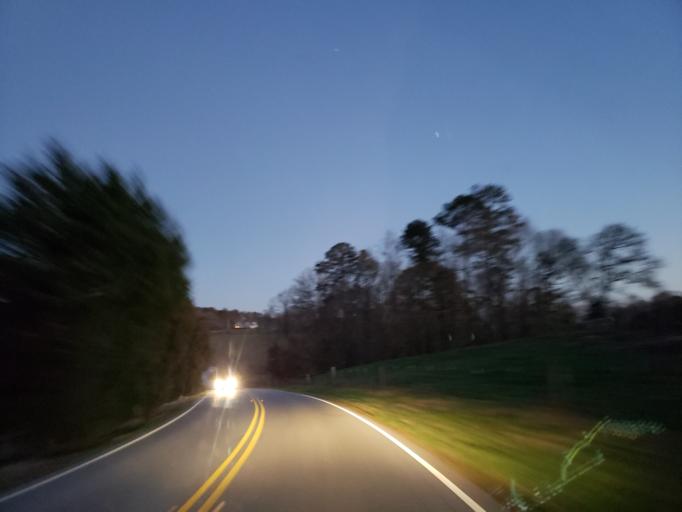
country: US
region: Georgia
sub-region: Bartow County
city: Emerson
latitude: 34.0639
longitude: -84.8116
